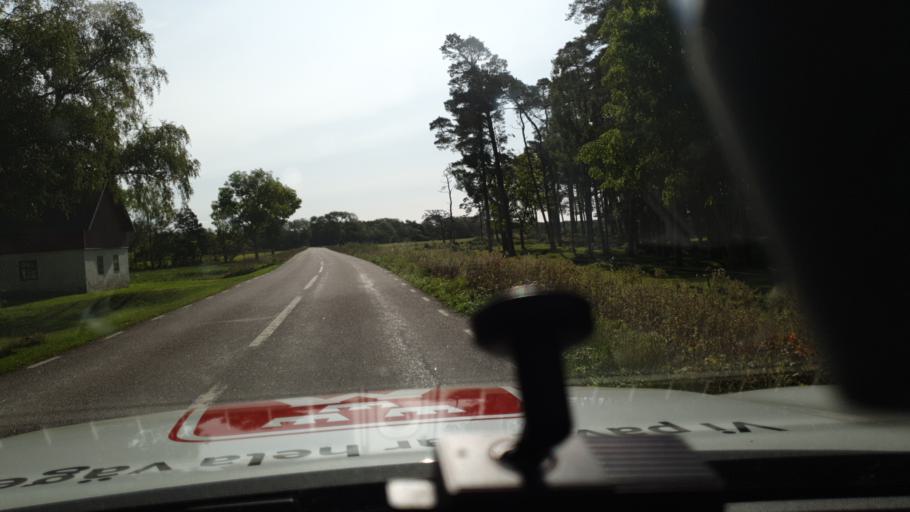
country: SE
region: Gotland
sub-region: Gotland
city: Hemse
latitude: 57.1088
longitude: 18.2916
